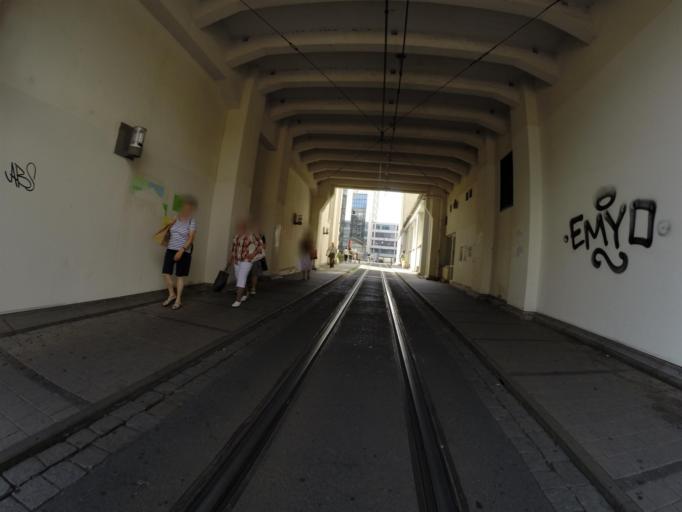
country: DE
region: Thuringia
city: Jena
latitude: 50.9274
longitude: 11.5829
